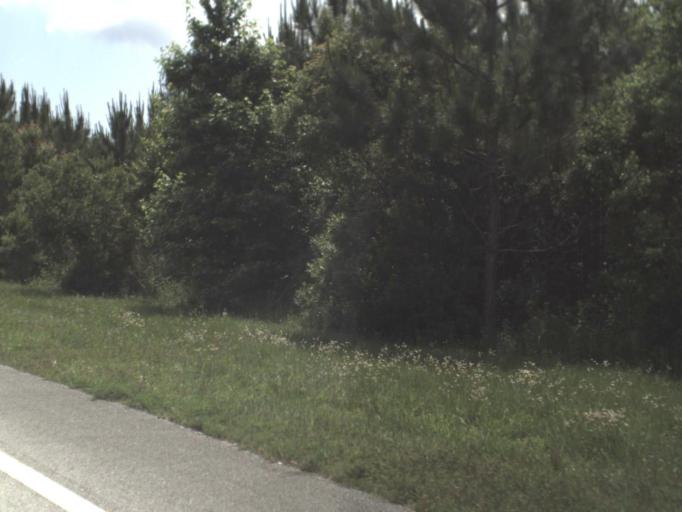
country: US
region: Florida
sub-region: Saint Johns County
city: Saint Augustine Shores
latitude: 29.7513
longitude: -81.3386
